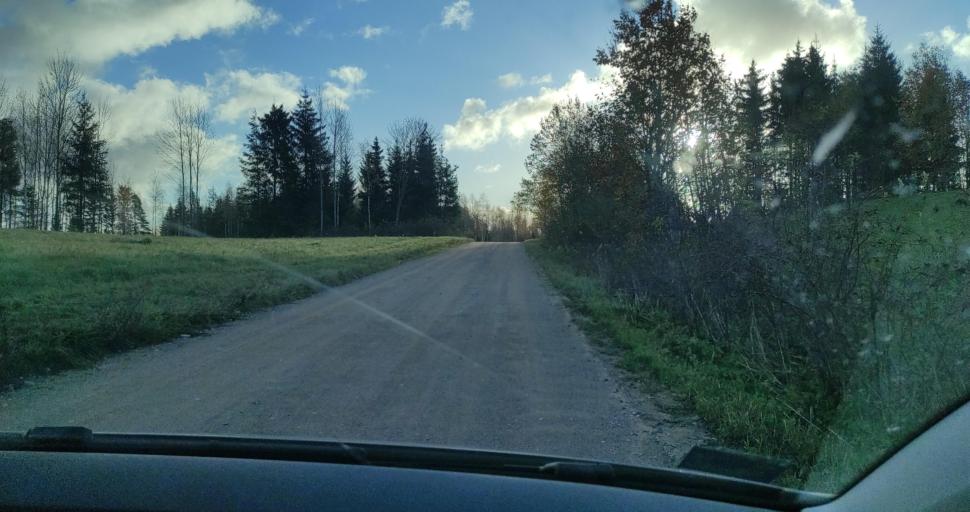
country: LV
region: Alsunga
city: Alsunga
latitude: 56.9494
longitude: 21.6321
